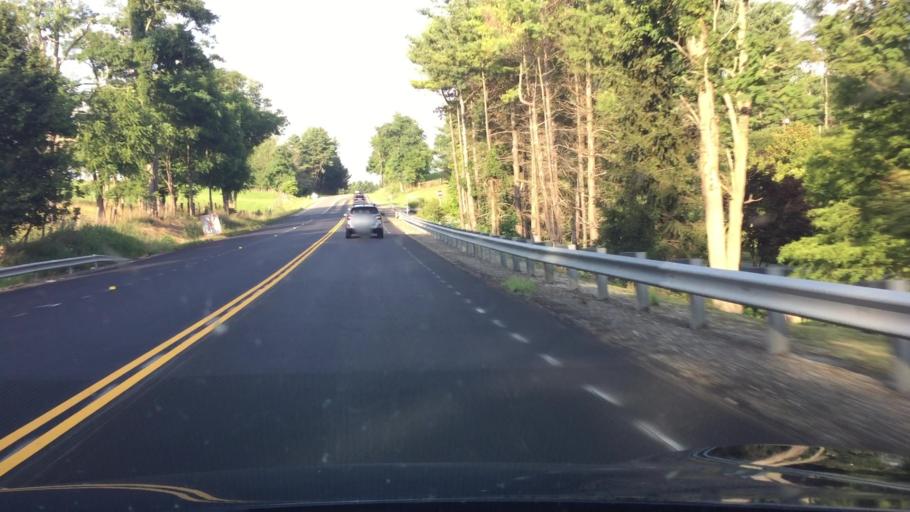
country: US
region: Virginia
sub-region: Montgomery County
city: Christiansburg
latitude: 37.1322
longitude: -80.4679
